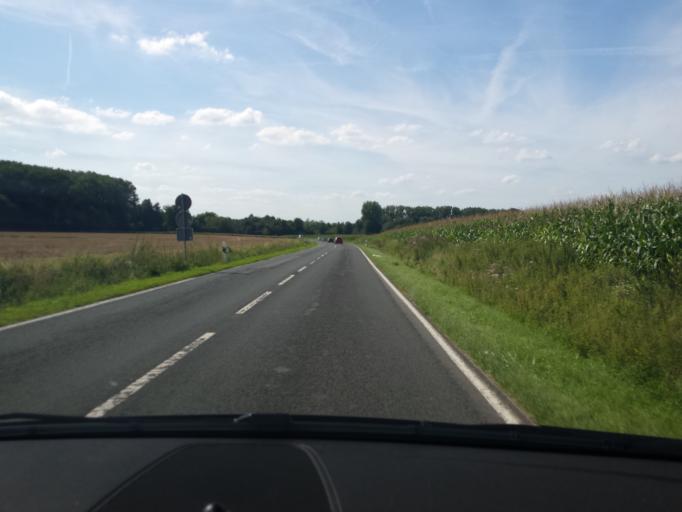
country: DE
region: North Rhine-Westphalia
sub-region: Regierungsbezirk Munster
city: Wadersloh
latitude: 51.6551
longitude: 8.2558
